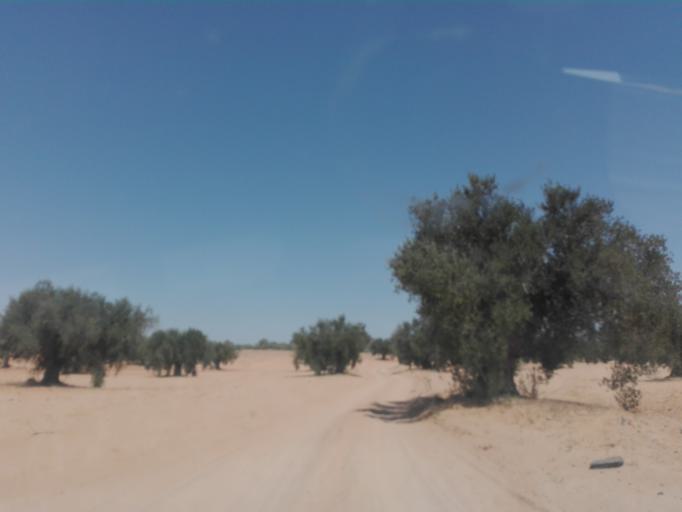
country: TN
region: Safaqis
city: Bi'r `Ali Bin Khalifah
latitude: 34.6491
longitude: 10.2768
